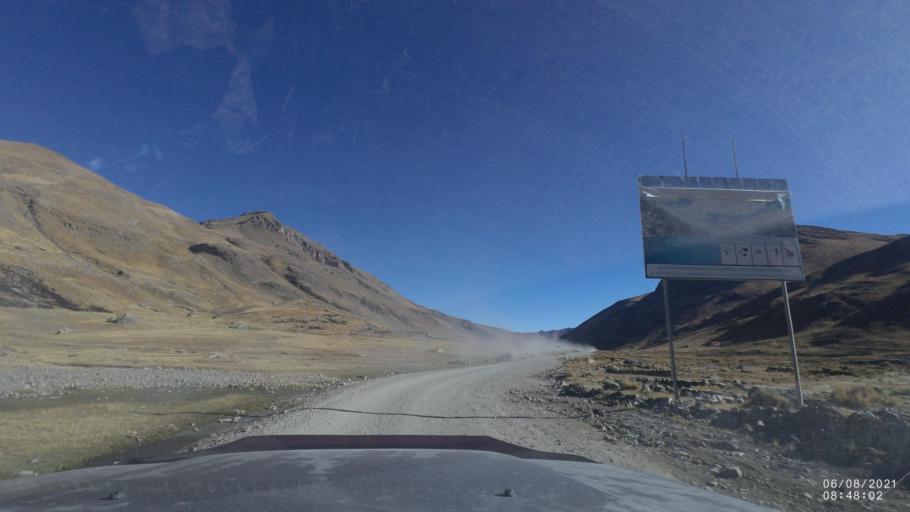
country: BO
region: Cochabamba
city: Sipe Sipe
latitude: -17.1652
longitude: -66.4282
